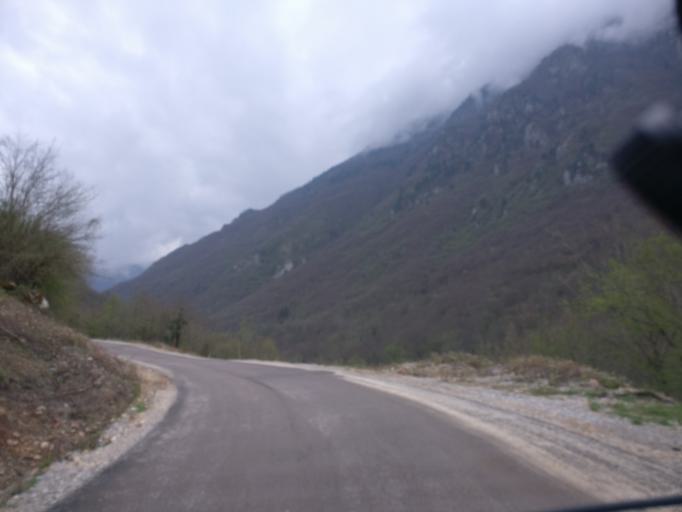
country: BA
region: Republika Srpska
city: Foca
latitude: 43.3596
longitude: 18.8123
